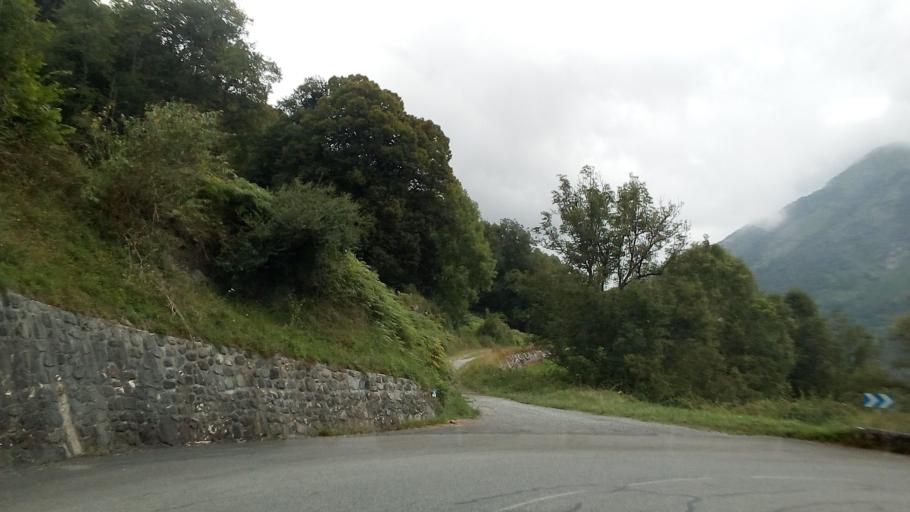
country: FR
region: Aquitaine
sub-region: Departement des Pyrenees-Atlantiques
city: Louvie-Juzon
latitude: 43.0617
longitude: -0.4378
